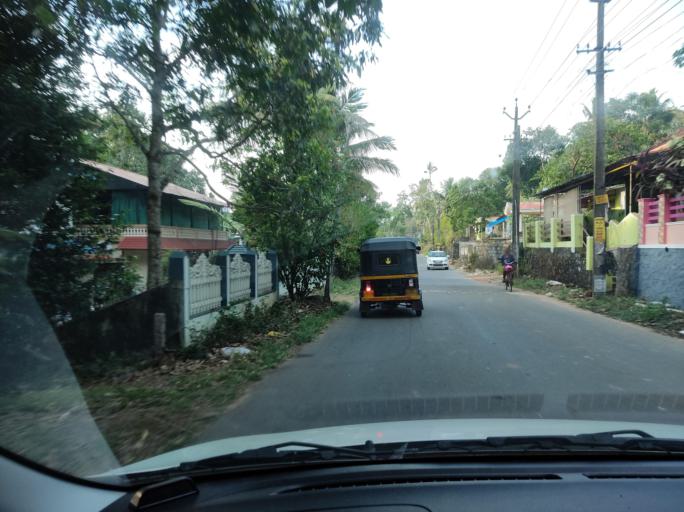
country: IN
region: Kerala
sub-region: Kottayam
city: Kottayam
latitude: 9.6497
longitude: 76.5095
